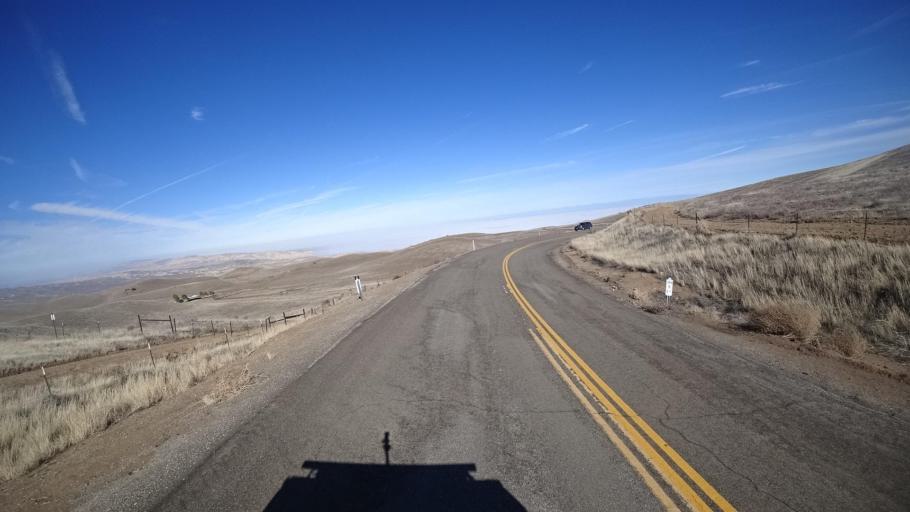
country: US
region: California
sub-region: Kern County
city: Maricopa
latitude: 34.9205
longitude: -119.4128
